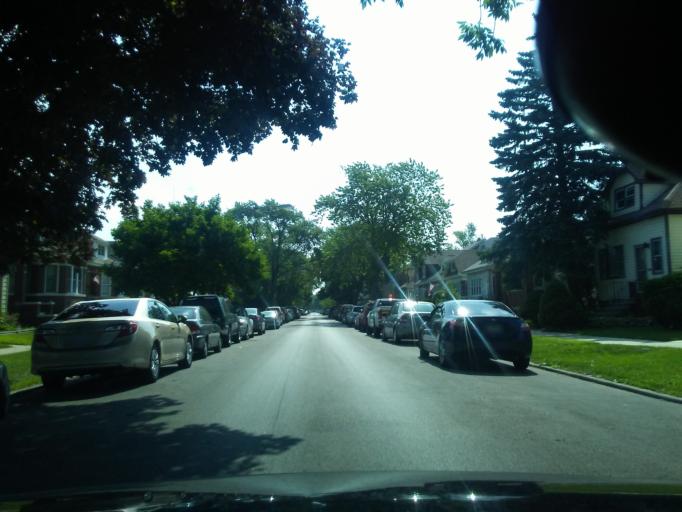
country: US
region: Illinois
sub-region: Cook County
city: Elmwood Park
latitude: 41.9368
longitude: -87.7608
